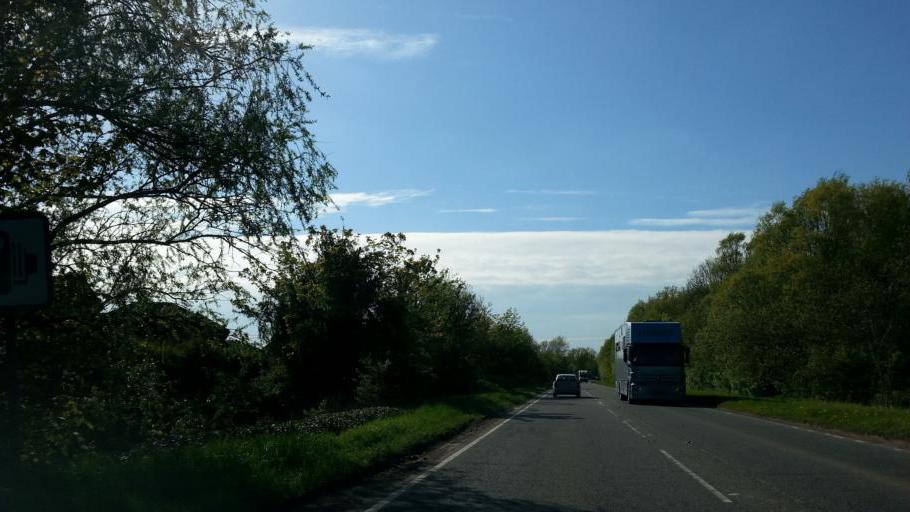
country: GB
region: England
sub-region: Cambridgeshire
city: Witchford
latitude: 52.3928
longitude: 0.1309
